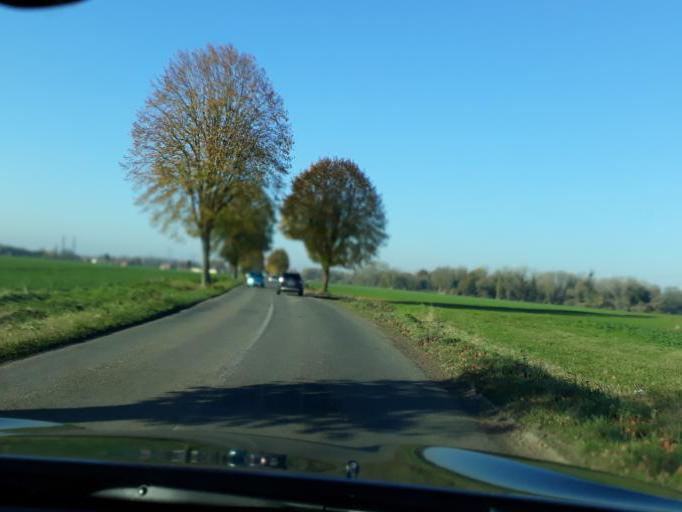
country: FR
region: Nord-Pas-de-Calais
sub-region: Departement du Nord
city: Guesnain
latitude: 50.3612
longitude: 3.1566
